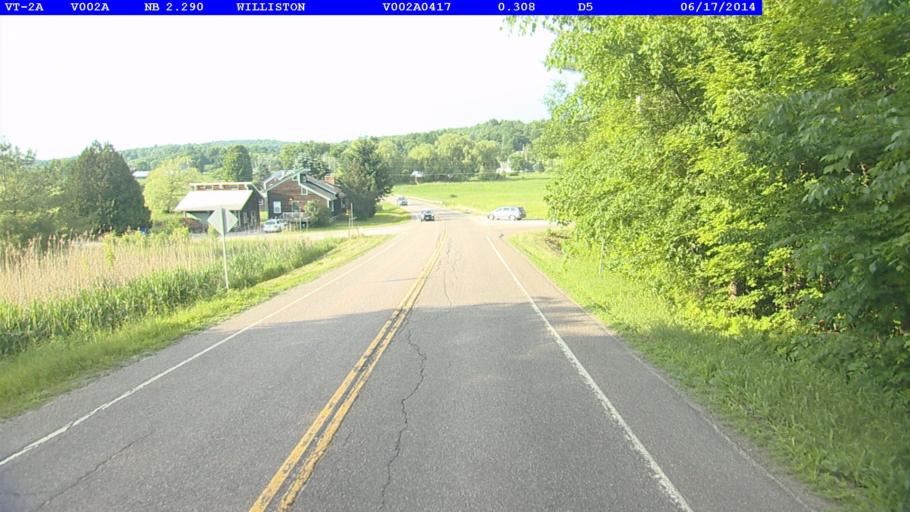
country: US
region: Vermont
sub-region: Chittenden County
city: Williston
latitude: 44.4024
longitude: -73.1268
